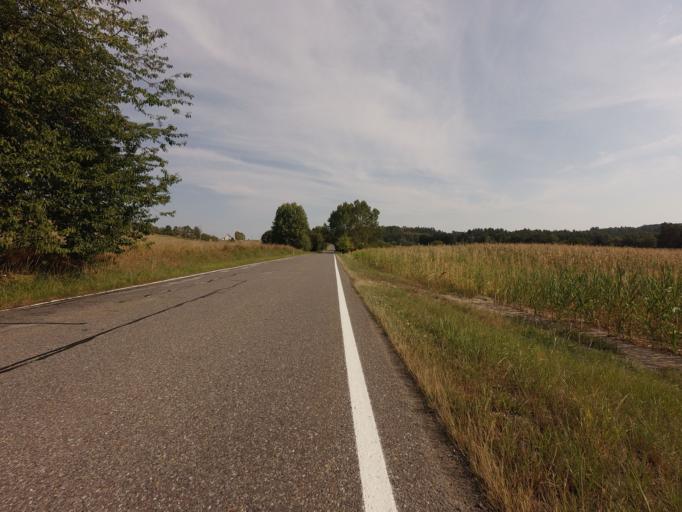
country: CZ
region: Jihocesky
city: Milevsko
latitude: 49.4970
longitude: 14.3618
